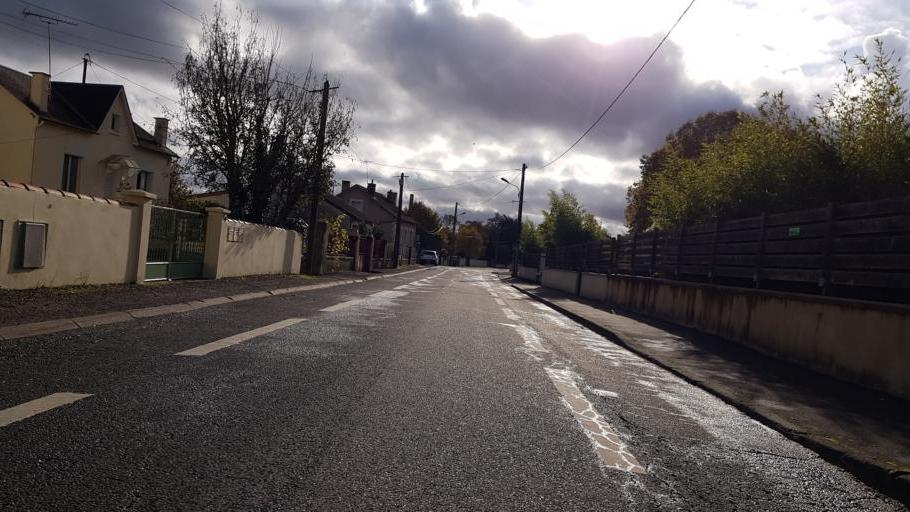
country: FR
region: Poitou-Charentes
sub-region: Departement de la Vienne
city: Chasseneuil-du-Poitou
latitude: 46.6551
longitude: 0.3781
